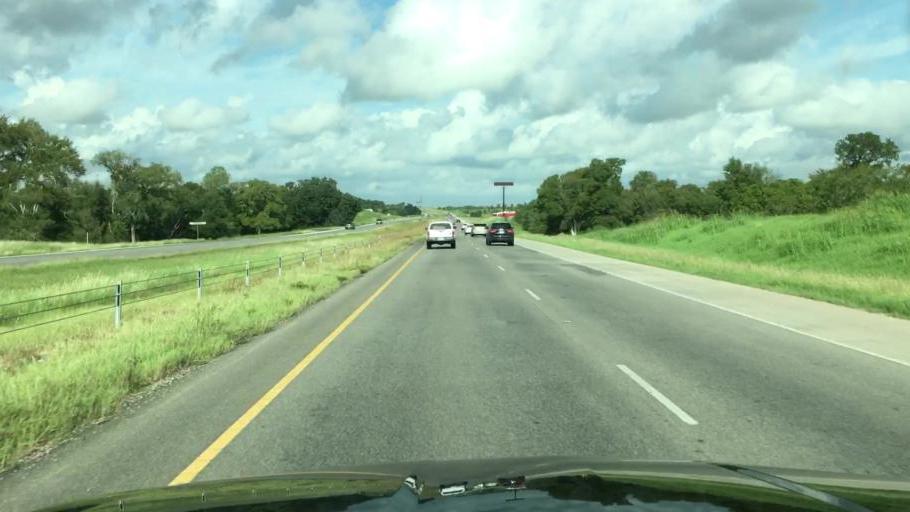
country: US
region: Texas
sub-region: Bastrop County
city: Wyldwood
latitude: 30.1626
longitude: -97.5055
